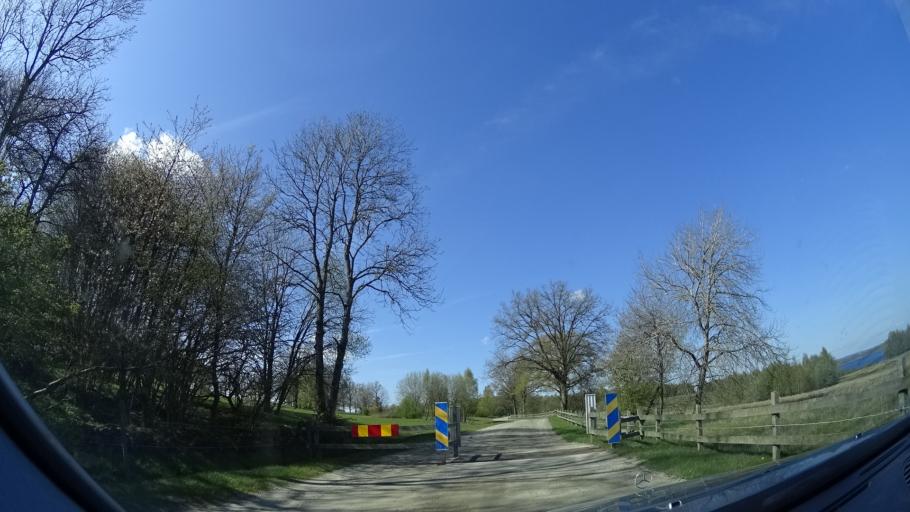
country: SE
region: Skane
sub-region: Hassleholms Kommun
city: Tormestorp
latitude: 56.1081
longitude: 13.6965
